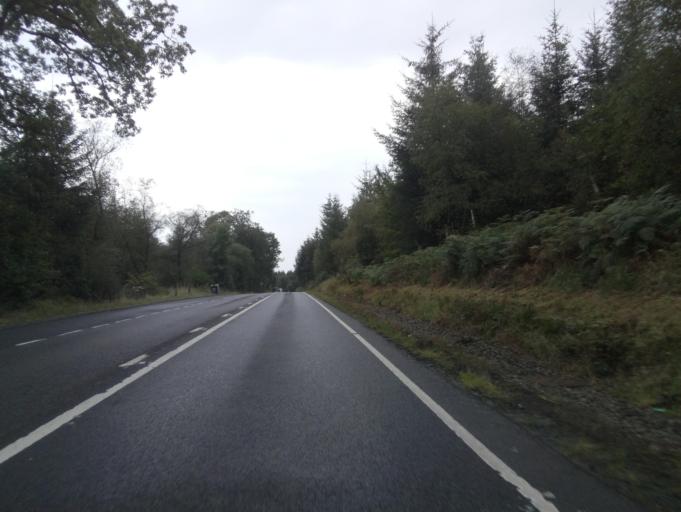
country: GB
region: Scotland
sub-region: Dumfries and Galloway
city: Lochmaben
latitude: 55.2203
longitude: -3.4673
